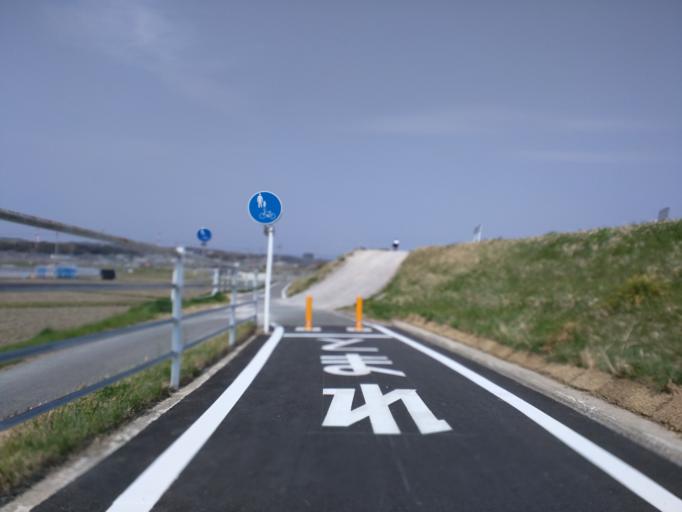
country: JP
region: Kyoto
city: Tanabe
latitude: 34.7876
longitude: 135.7978
